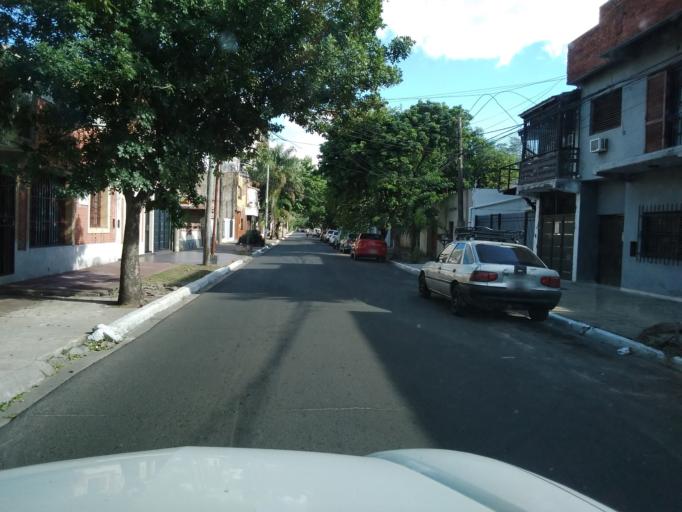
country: AR
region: Corrientes
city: Corrientes
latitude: -27.4777
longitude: -58.8315
